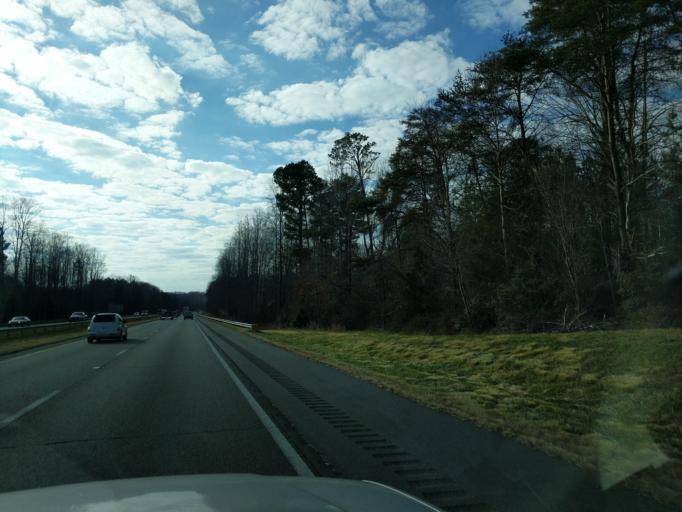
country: US
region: North Carolina
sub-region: Catawba County
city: Claremont
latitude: 35.7320
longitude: -81.1094
